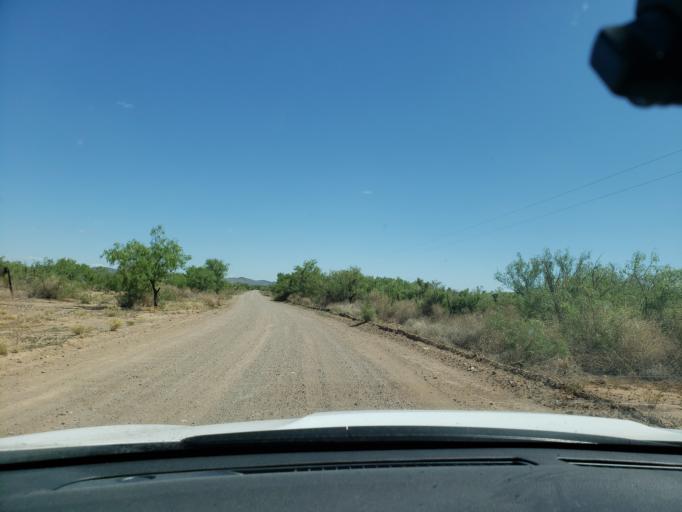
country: US
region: Texas
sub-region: Presidio County
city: Marfa
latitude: 30.5944
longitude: -104.4894
